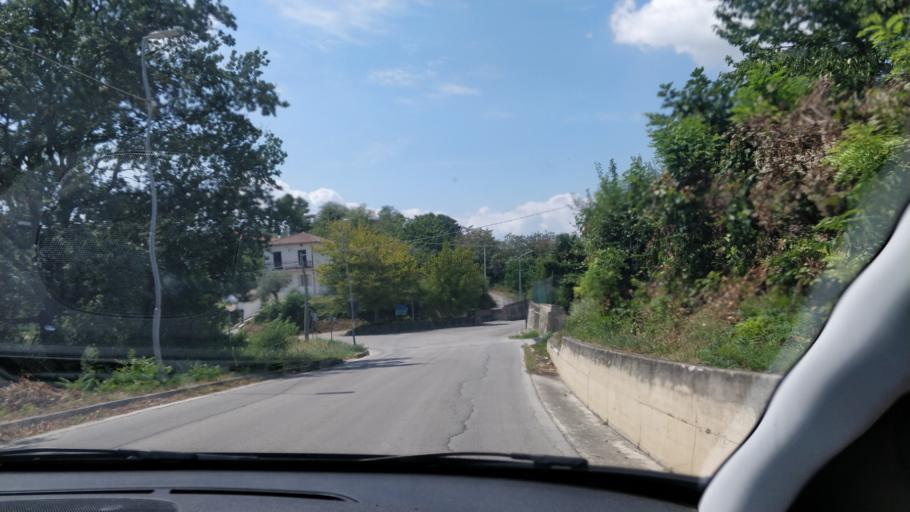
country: IT
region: Abruzzo
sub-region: Provincia di Chieti
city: Sambuceto
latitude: 42.4046
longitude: 14.1981
